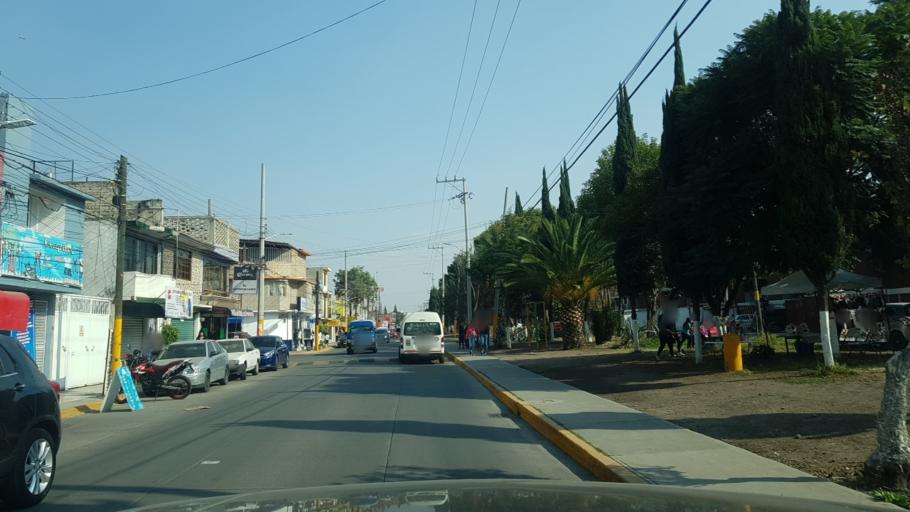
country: MX
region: Mexico
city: Santiago Teyahualco
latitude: 19.6523
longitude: -99.1174
